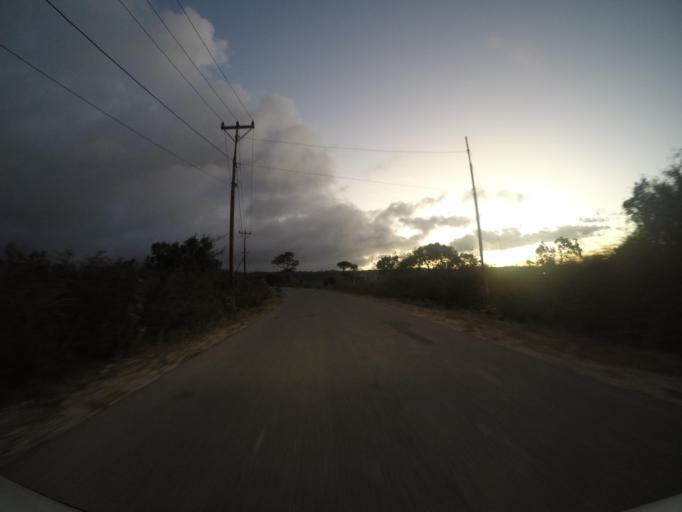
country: TL
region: Lautem
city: Lospalos
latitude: -8.3733
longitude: 127.0175
